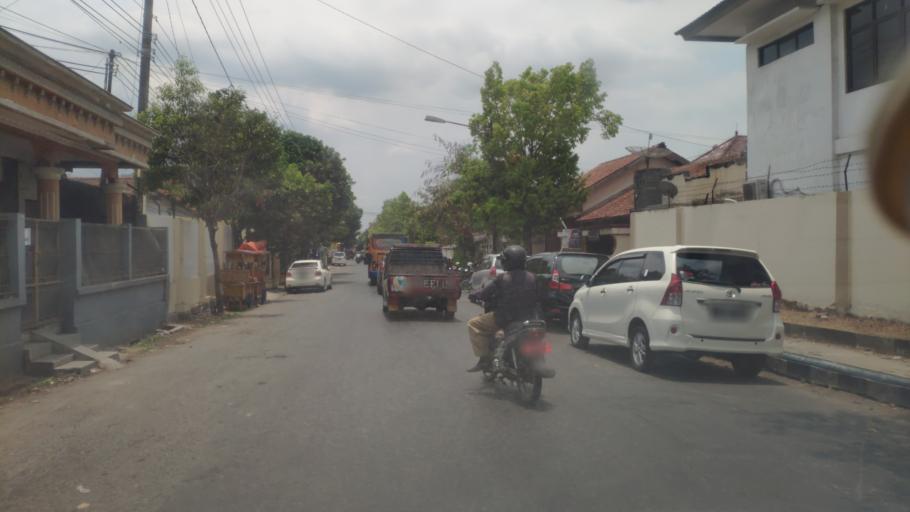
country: ID
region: Central Java
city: Wonosobo
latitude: -7.3973
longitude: 109.7007
